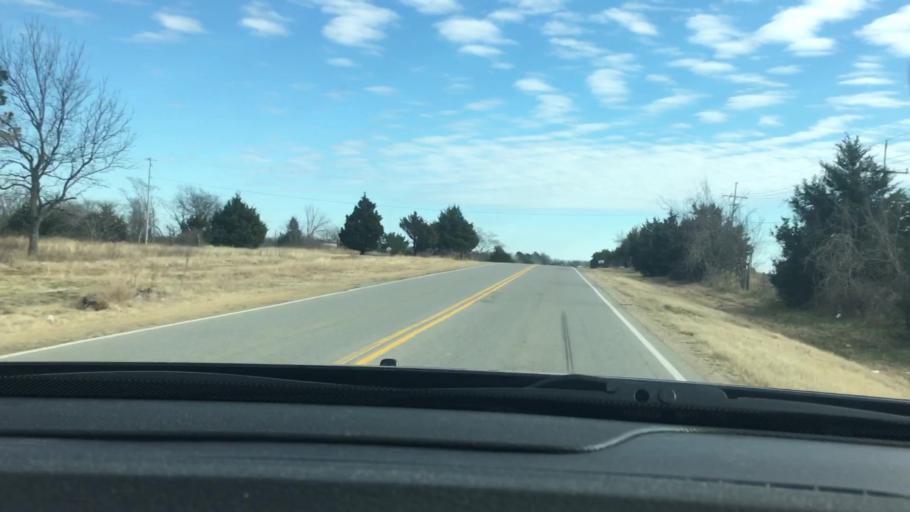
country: US
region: Oklahoma
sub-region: Pontotoc County
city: Ada
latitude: 34.7877
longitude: -96.7967
